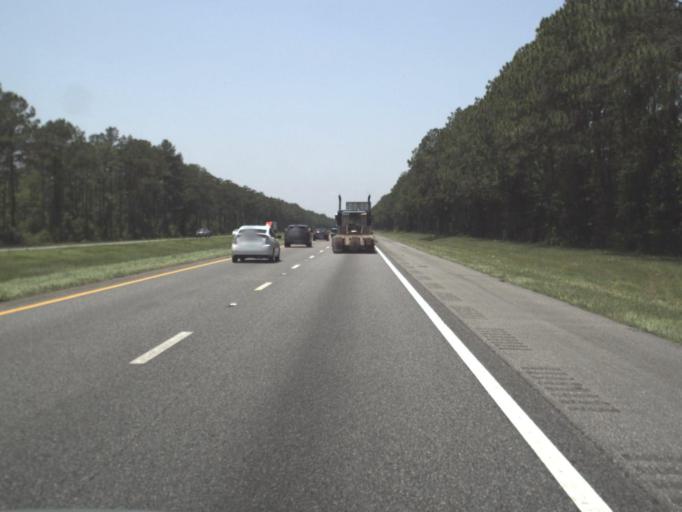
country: US
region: Florida
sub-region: Baker County
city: Macclenny
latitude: 30.2544
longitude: -82.3407
